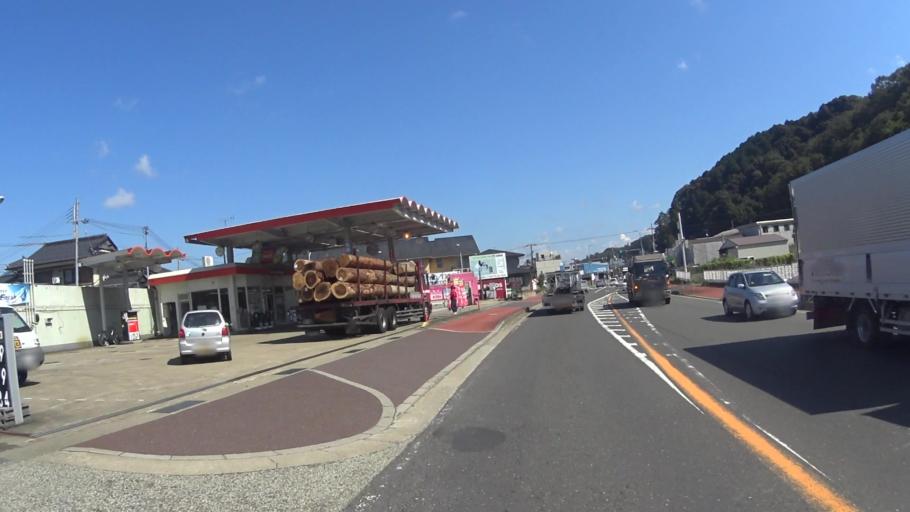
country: JP
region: Kyoto
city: Ayabe
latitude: 35.2997
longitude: 135.2675
